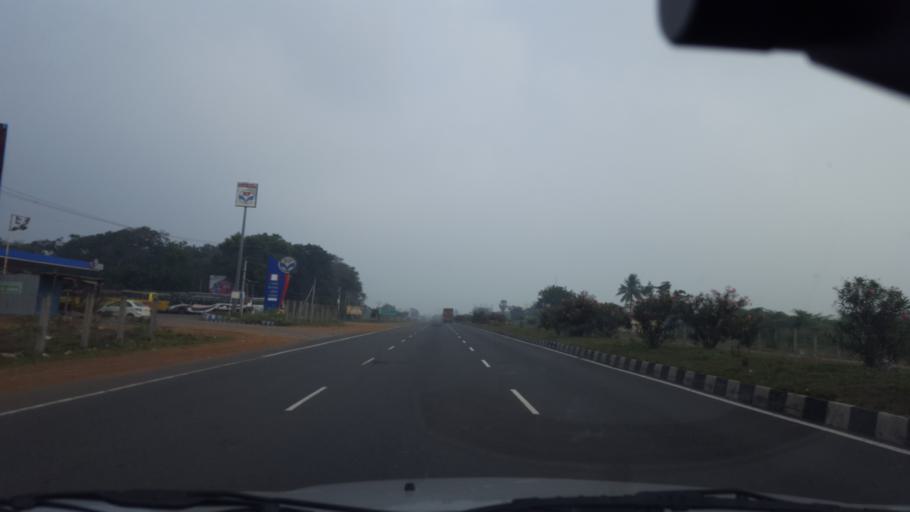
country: IN
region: Andhra Pradesh
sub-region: Prakasam
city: Addanki
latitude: 15.6779
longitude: 80.0172
